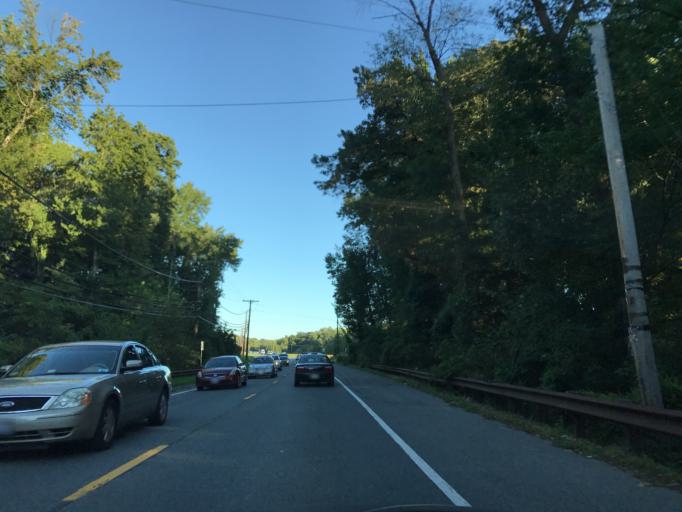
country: US
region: Maryland
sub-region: Prince George's County
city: Beltsville
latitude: 39.0160
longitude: -76.8974
